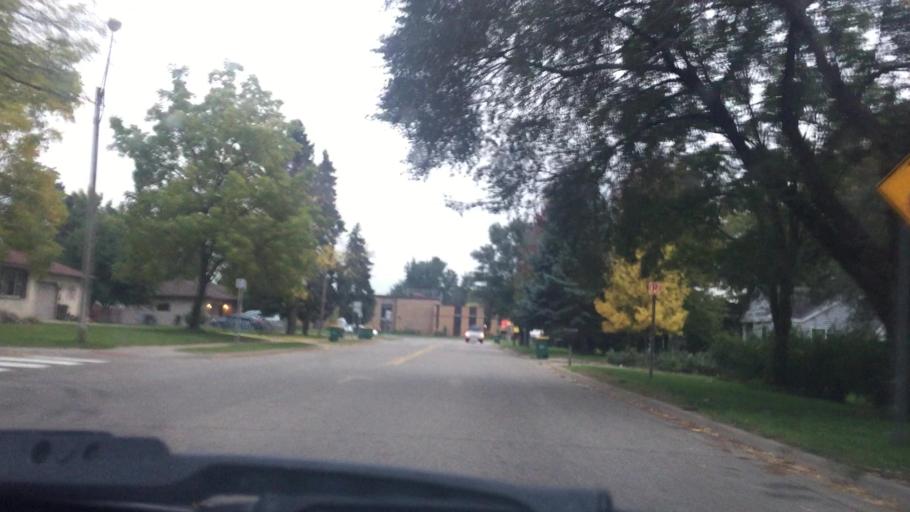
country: US
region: Minnesota
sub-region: Anoka County
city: Spring Lake Park
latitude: 45.1090
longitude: -93.2484
